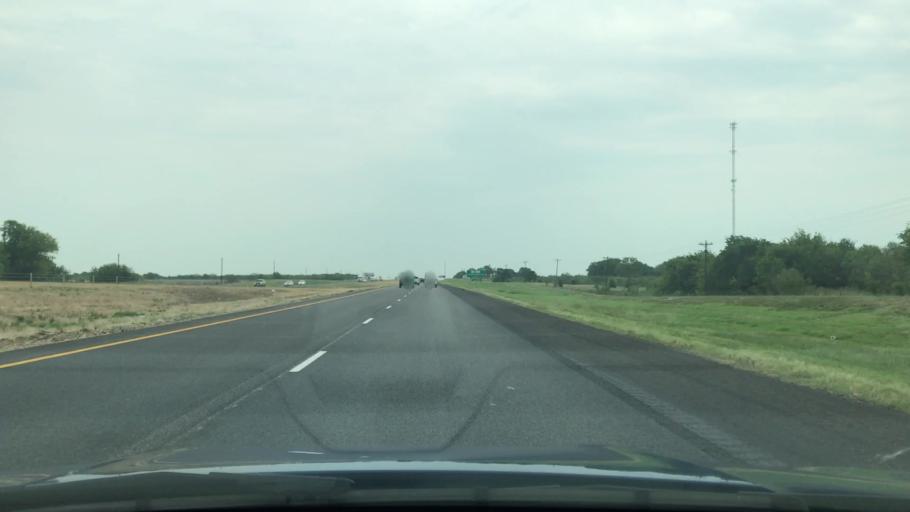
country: US
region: Texas
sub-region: Kaufman County
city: Terrell
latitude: 32.6863
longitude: -96.2170
